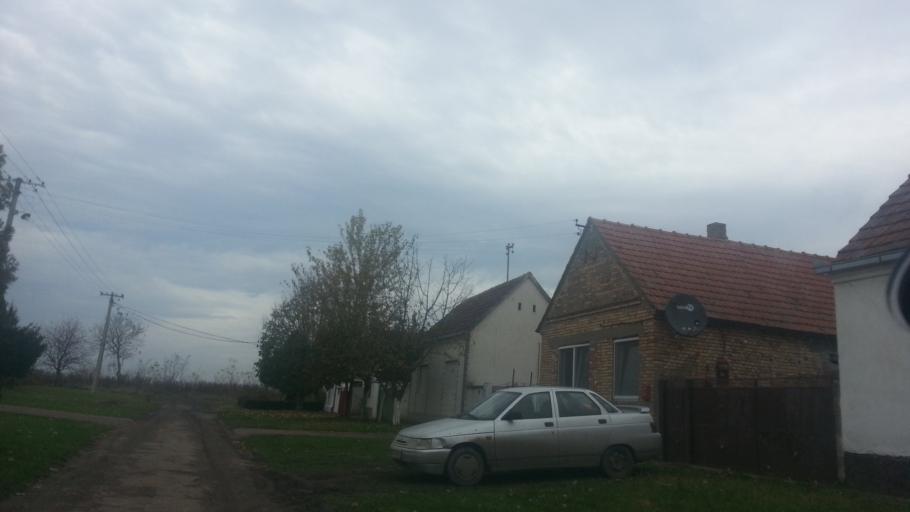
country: RS
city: Golubinci
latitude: 44.9974
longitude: 20.0649
